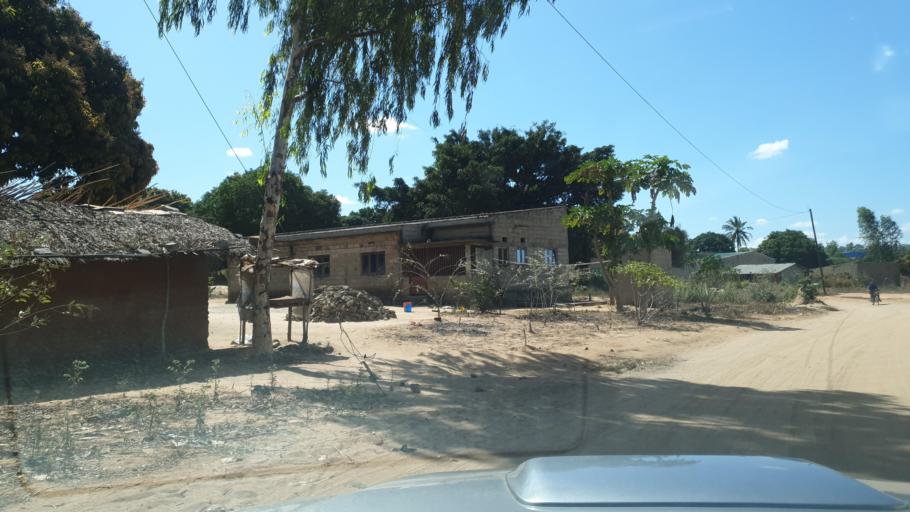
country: MZ
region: Nampula
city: Nampula
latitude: -15.1008
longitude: 39.2069
